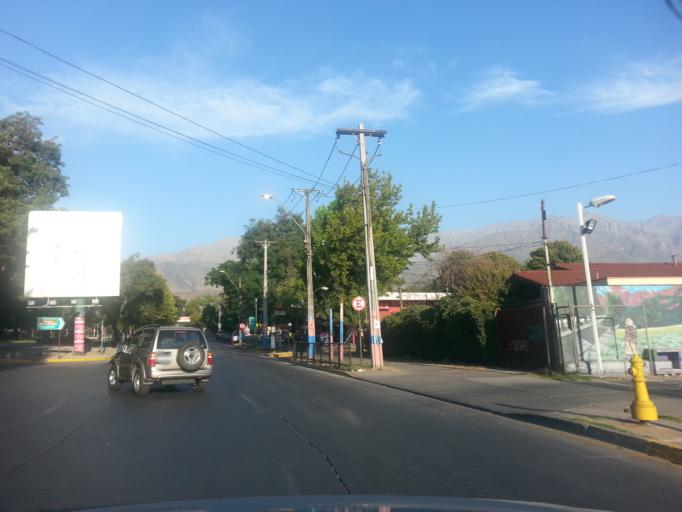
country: CL
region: Santiago Metropolitan
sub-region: Provincia de Santiago
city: Villa Presidente Frei, Nunoa, Santiago, Chile
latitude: -33.4307
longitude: -70.5545
